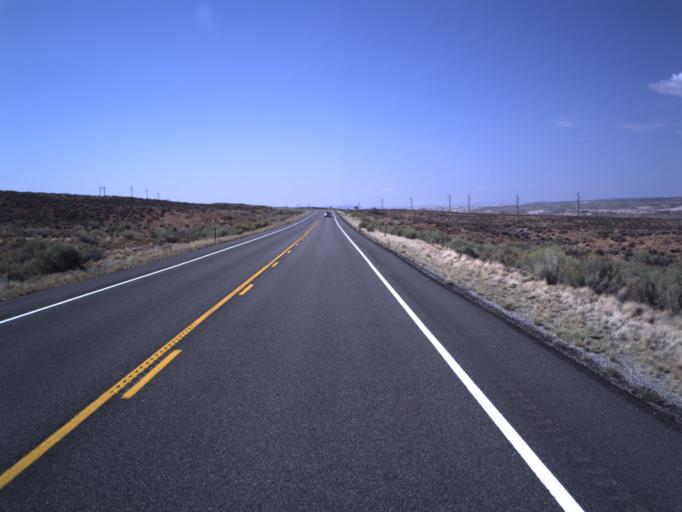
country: US
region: Utah
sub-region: San Juan County
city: Blanding
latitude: 37.3602
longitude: -109.5138
